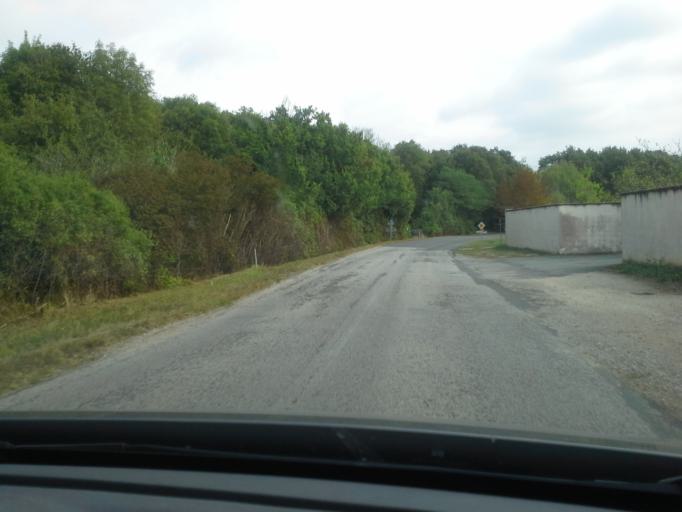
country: FR
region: Centre
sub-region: Departement du Loir-et-Cher
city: Herbault
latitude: 47.5870
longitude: 1.2012
